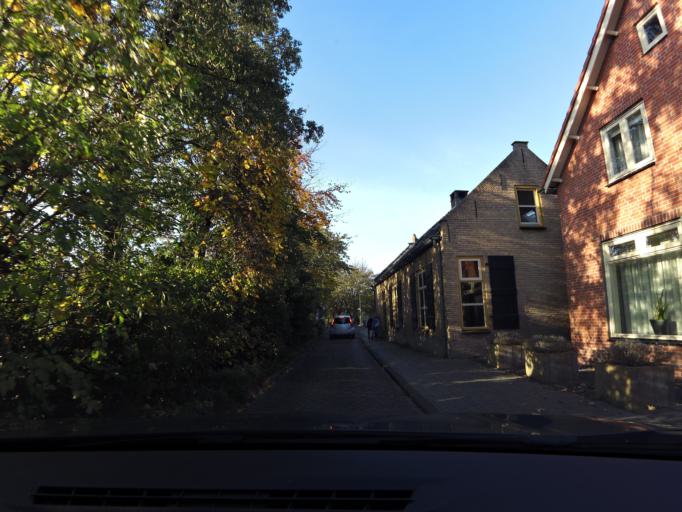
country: NL
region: North Brabant
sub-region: Gemeente Made en Drimmelen
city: Drimmelen
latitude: 51.7086
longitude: 4.8040
